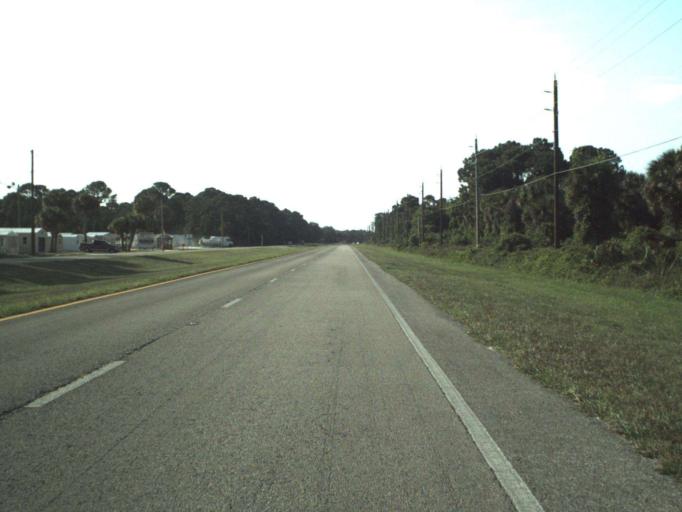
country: US
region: Florida
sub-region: Volusia County
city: Oak Hill
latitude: 28.8865
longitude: -80.8574
